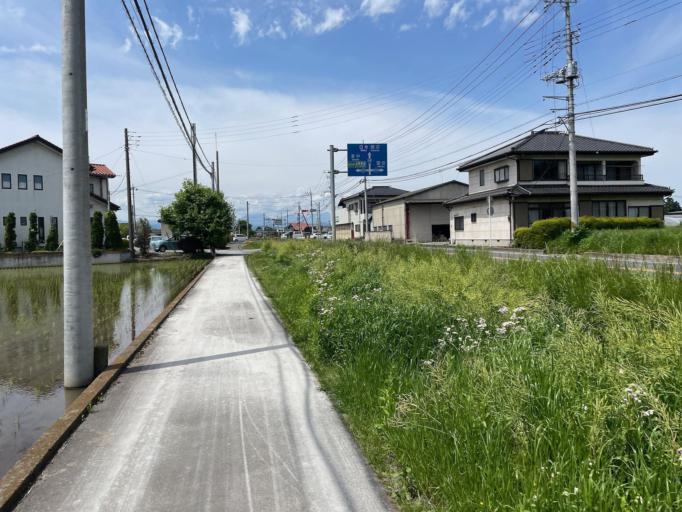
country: JP
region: Tochigi
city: Mibu
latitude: 36.4449
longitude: 139.7825
